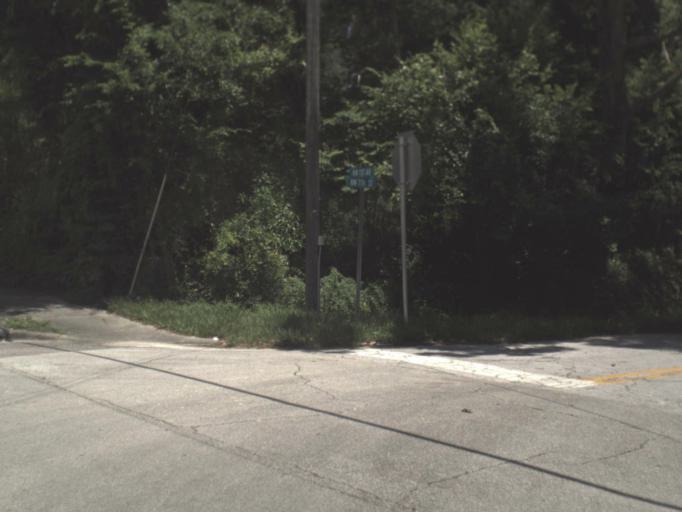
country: US
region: Florida
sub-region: Alachua County
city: High Springs
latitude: 29.8301
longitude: -82.6040
